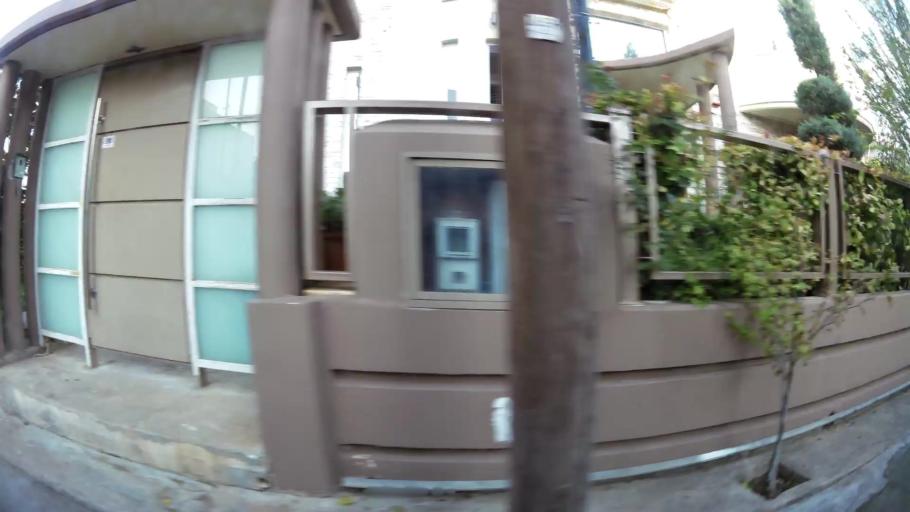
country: GR
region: Attica
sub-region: Nomarchia Dytikis Attikis
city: Zefyri
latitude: 38.0511
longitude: 23.7233
